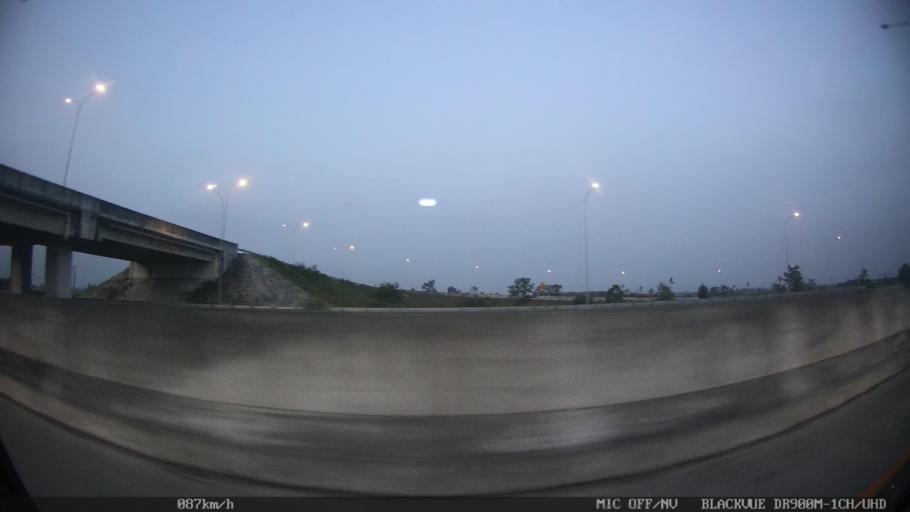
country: ID
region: Lampung
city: Sidorejo
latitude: -5.6091
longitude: 105.5572
